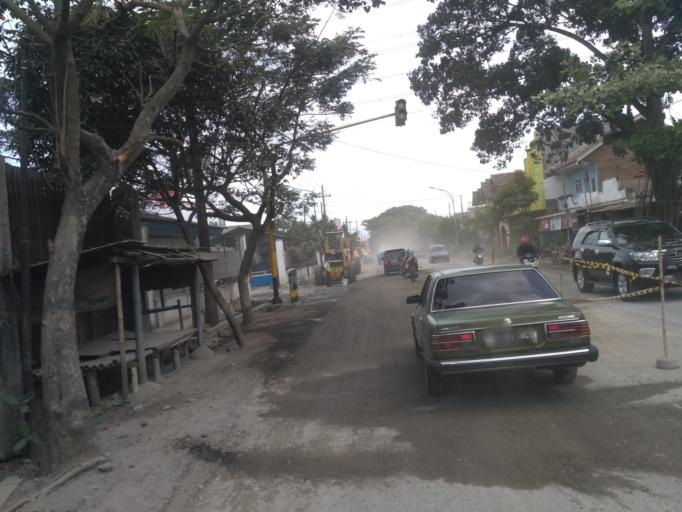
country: ID
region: East Java
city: Kebonsari
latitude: -8.0256
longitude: 112.6275
